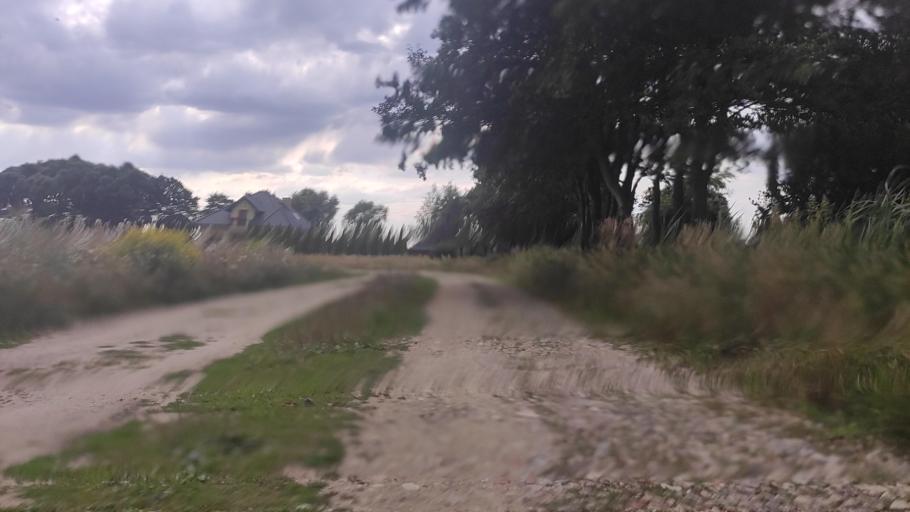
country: PL
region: Greater Poland Voivodeship
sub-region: Powiat poznanski
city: Swarzedz
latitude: 52.3881
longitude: 17.0923
